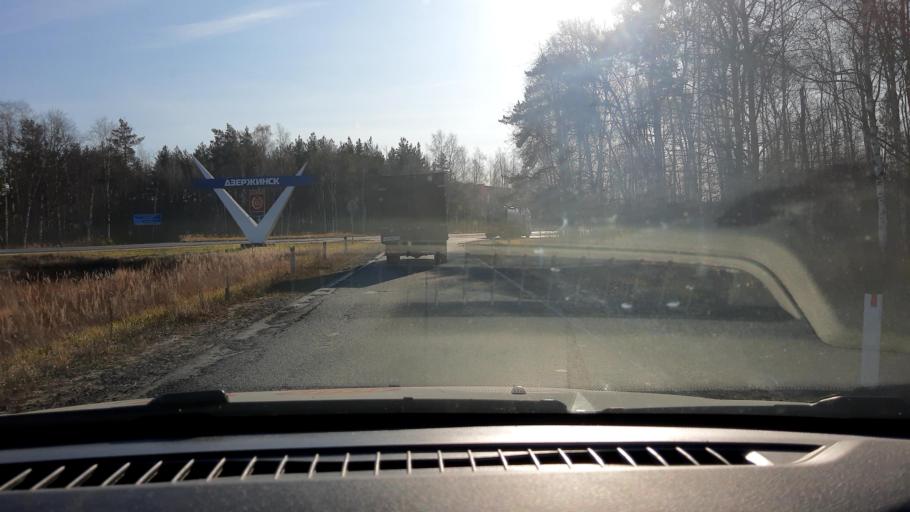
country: RU
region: Nizjnij Novgorod
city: Dzerzhinsk
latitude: 56.2970
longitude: 43.4757
